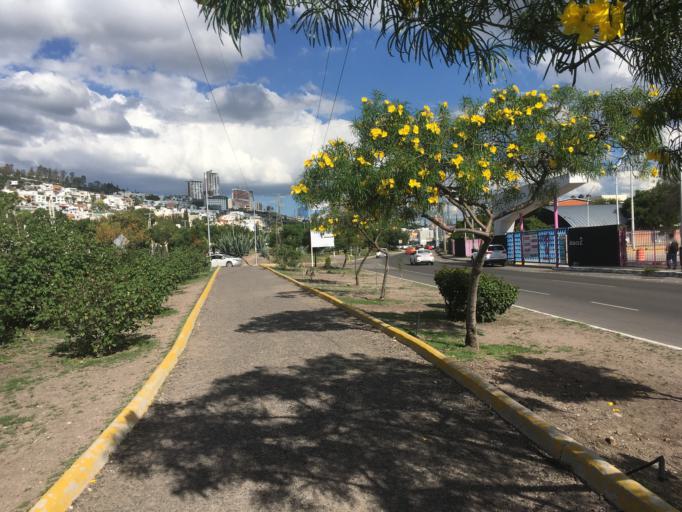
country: MX
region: Queretaro
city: San Jose el Alto
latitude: 20.6225
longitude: -100.3935
